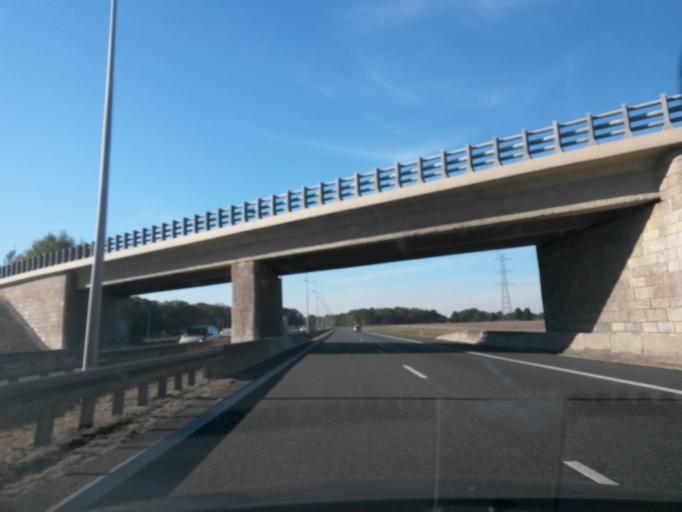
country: PL
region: Opole Voivodeship
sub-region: Powiat brzeski
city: Olszanka
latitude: 50.7633
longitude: 17.4170
